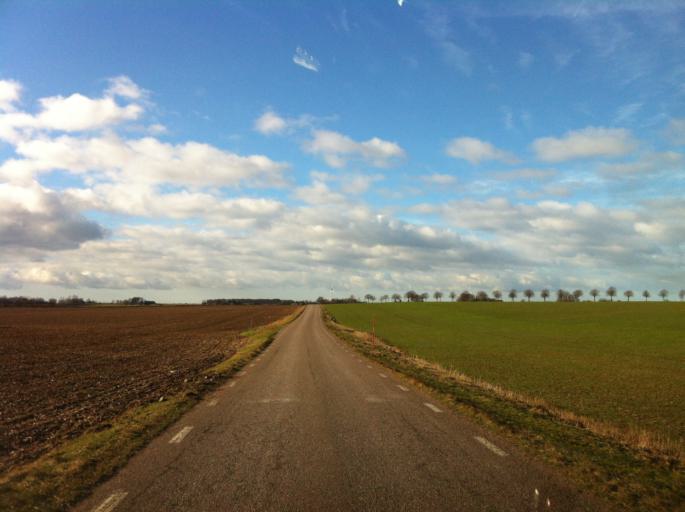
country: SE
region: Skane
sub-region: Landskrona
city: Asmundtorp
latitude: 55.9347
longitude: 13.0112
